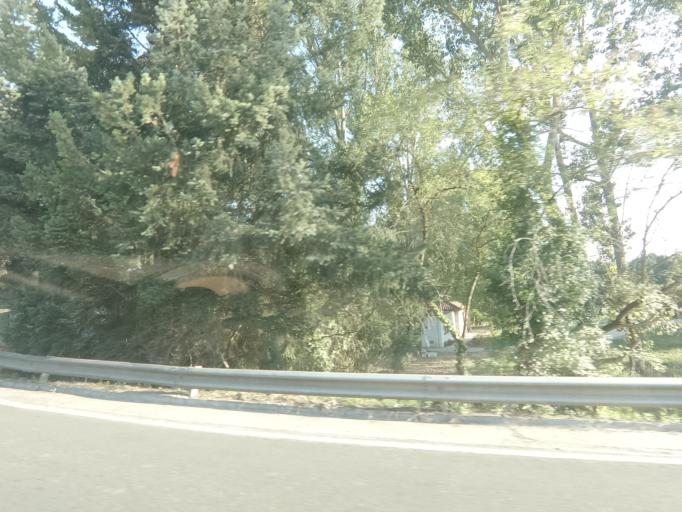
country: PT
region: Vila Real
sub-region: Vila Real
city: Vila Real
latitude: 41.2967
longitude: -7.7090
